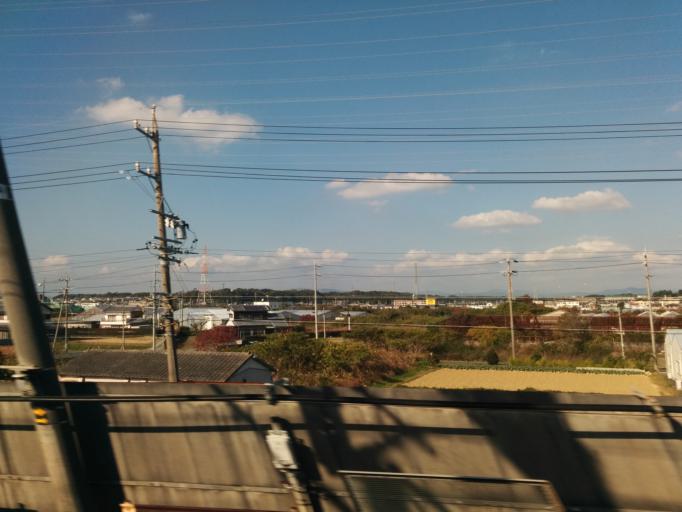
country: JP
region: Shizuoka
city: Hamamatsu
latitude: 34.6936
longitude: 137.6717
